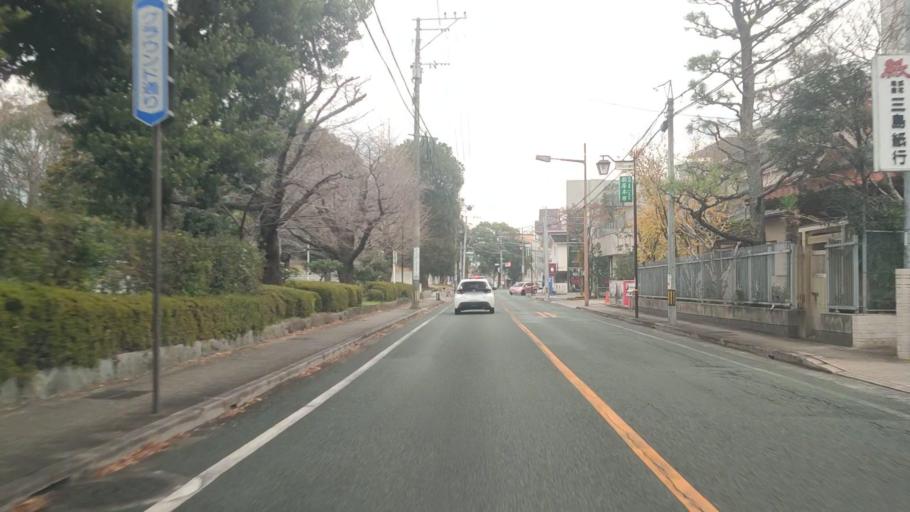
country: JP
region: Kumamoto
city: Kumamoto
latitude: 32.7918
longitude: 130.7406
